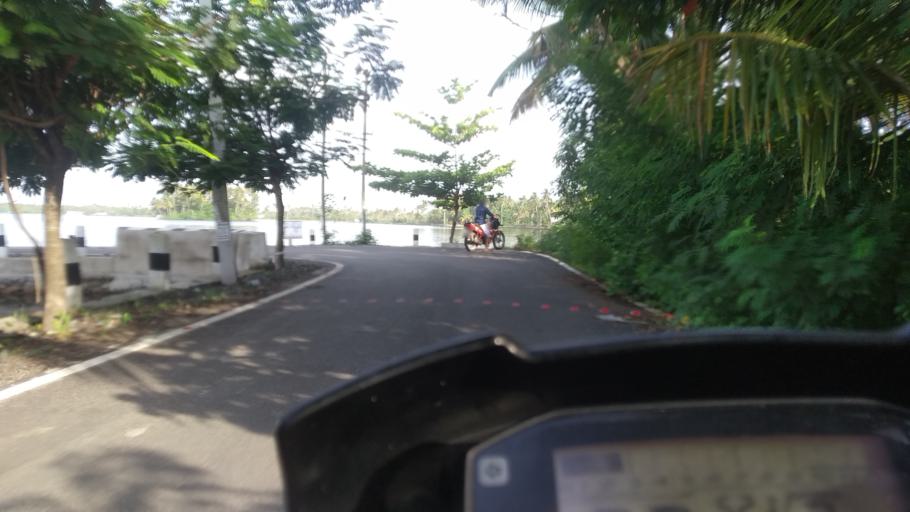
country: IN
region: Kerala
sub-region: Ernakulam
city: Elur
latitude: 10.0962
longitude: 76.1912
